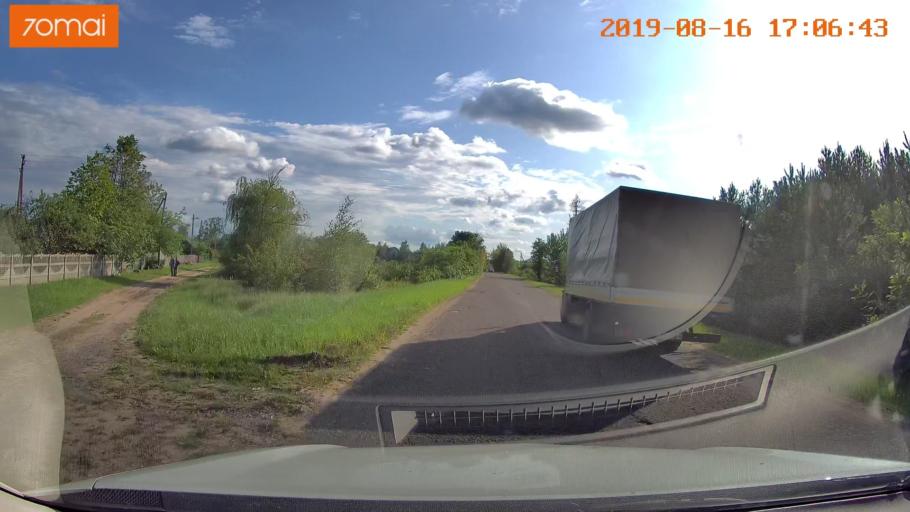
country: BY
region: Mogilev
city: Hlusha
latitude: 53.2238
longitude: 28.9296
